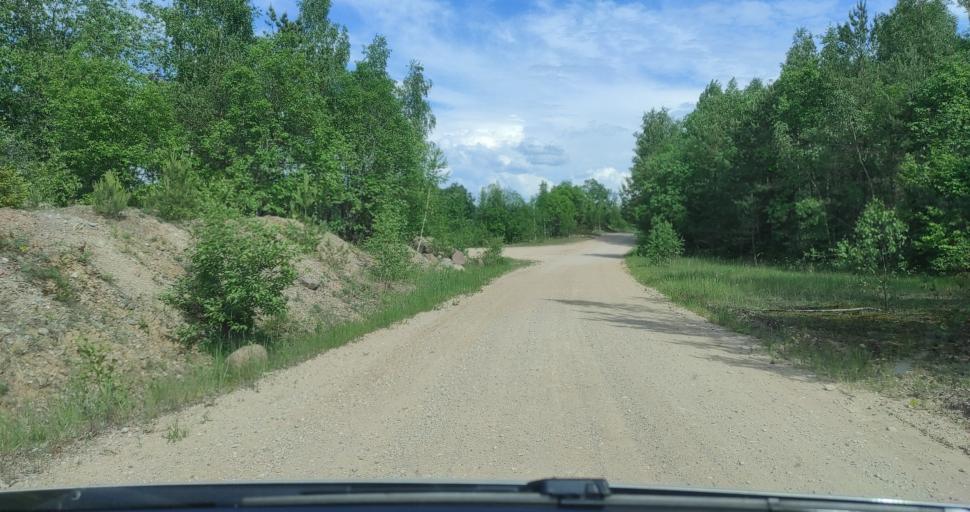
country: LV
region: Kuldigas Rajons
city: Kuldiga
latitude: 56.8602
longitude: 21.9160
